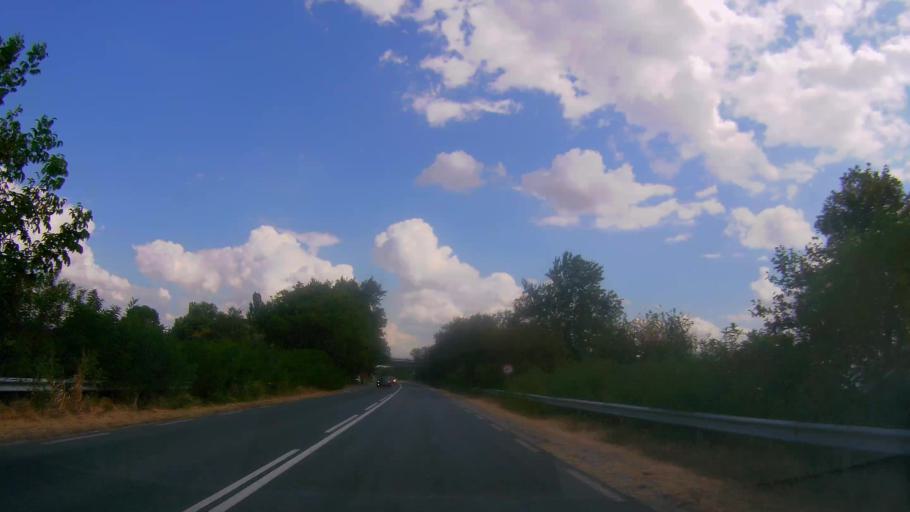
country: BG
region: Sliven
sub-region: Obshtina Sliven
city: Kermen
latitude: 42.6313
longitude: 26.1770
